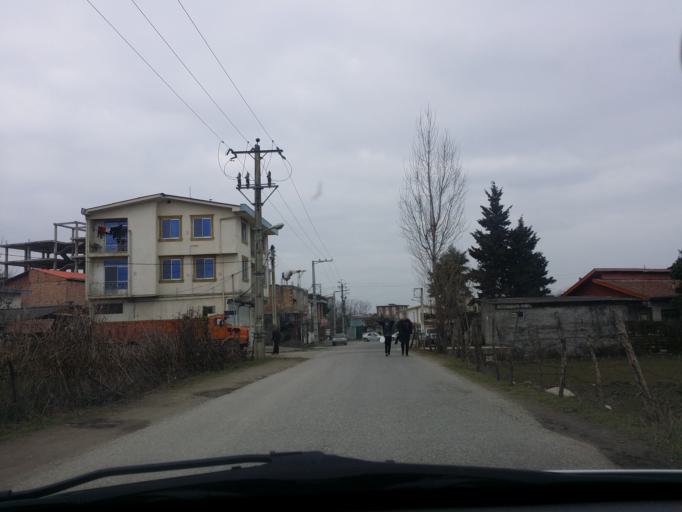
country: IR
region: Mazandaran
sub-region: Nowshahr
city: Nowshahr
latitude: 36.6438
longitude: 51.4820
